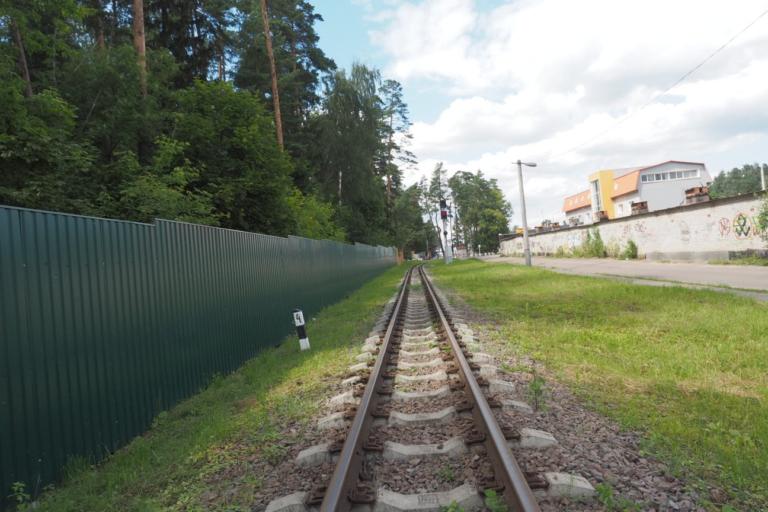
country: RU
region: Moskovskaya
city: Zhukovskiy
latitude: 55.5994
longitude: 38.1401
